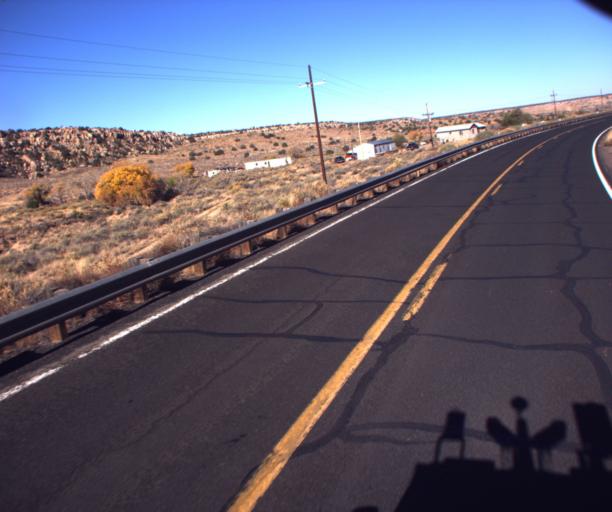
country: US
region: Arizona
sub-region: Navajo County
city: First Mesa
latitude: 35.8179
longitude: -110.2160
